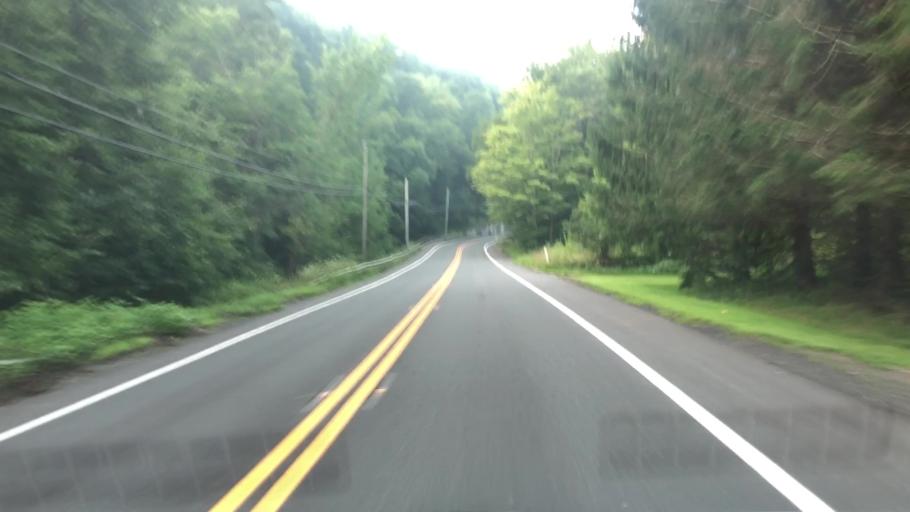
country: US
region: Massachusetts
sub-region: Franklin County
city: Buckland
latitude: 42.5607
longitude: -72.8043
